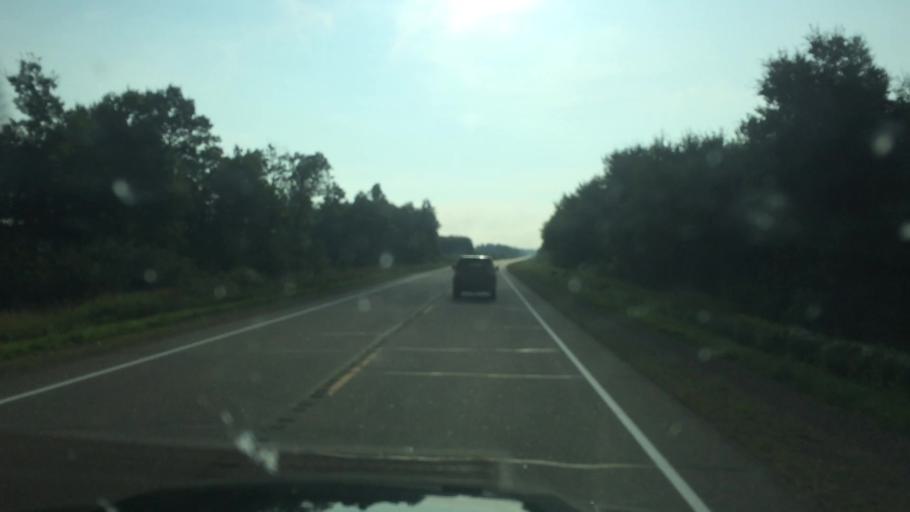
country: US
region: Wisconsin
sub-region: Langlade County
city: Antigo
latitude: 45.1467
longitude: -89.3462
